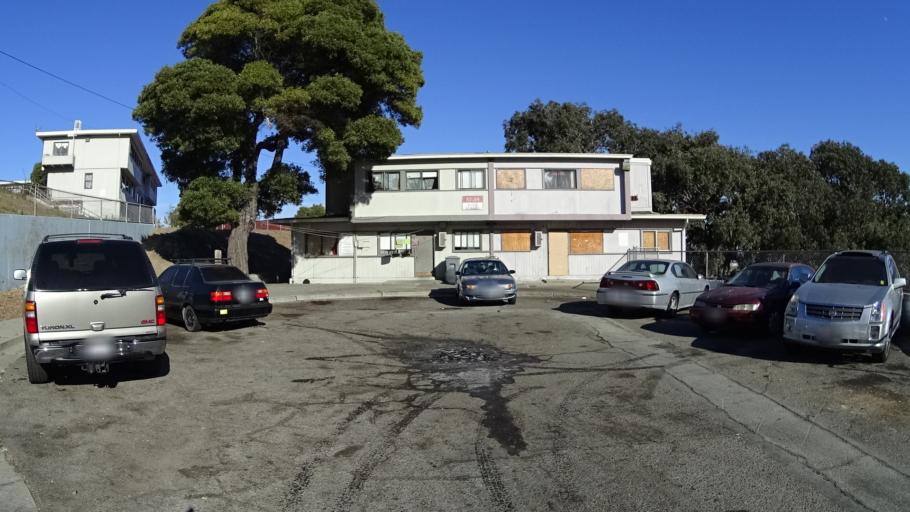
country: US
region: California
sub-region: San Francisco County
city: San Francisco
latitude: 37.7345
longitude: -122.3787
